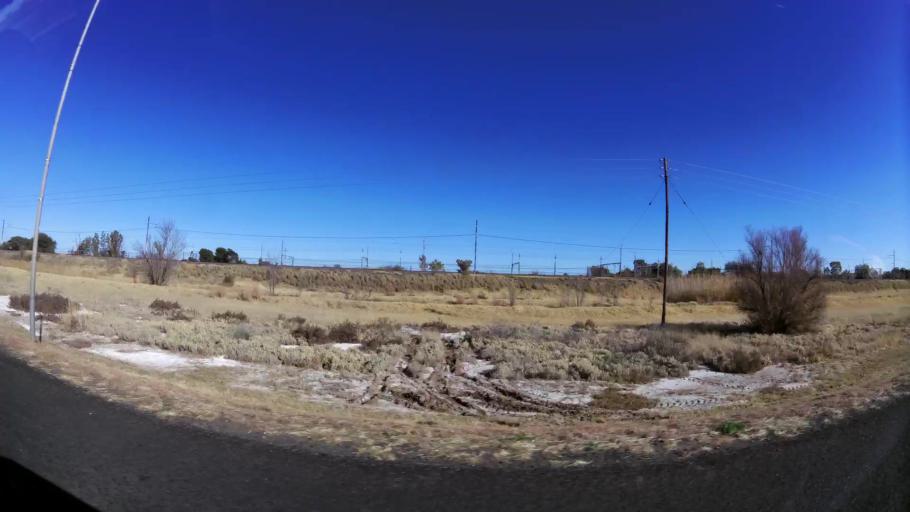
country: ZA
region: Northern Cape
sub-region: Frances Baard District Municipality
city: Kimberley
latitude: -28.6979
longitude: 24.7776
